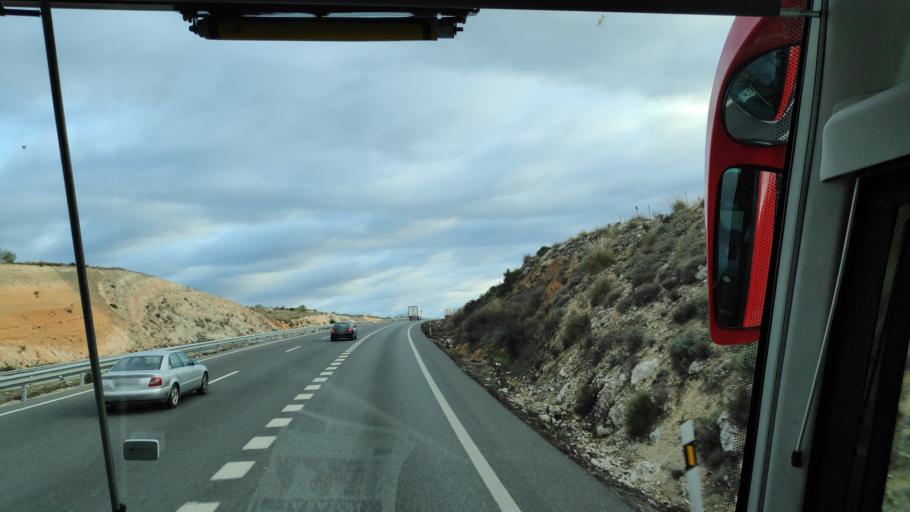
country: ES
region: Madrid
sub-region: Provincia de Madrid
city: Villarejo de Salvanes
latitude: 40.1916
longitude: -3.3005
